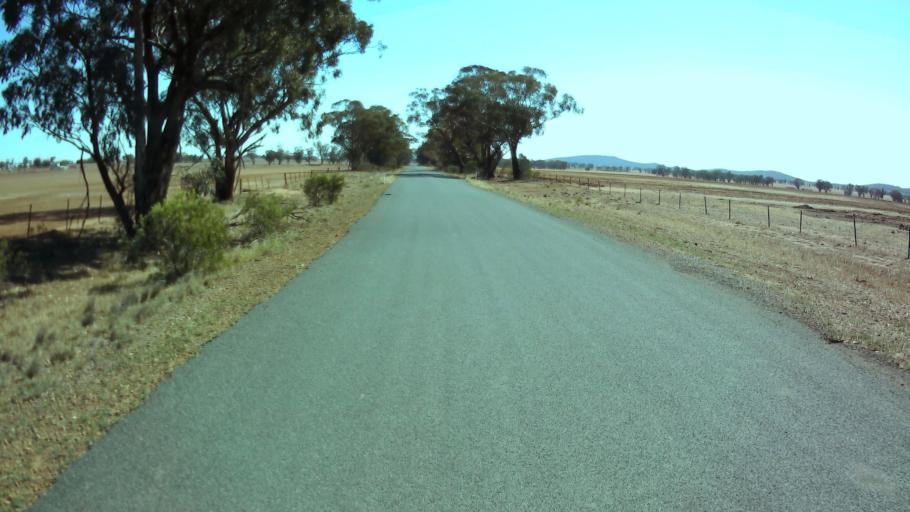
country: AU
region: New South Wales
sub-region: Weddin
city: Grenfell
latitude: -33.7475
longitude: 147.8767
